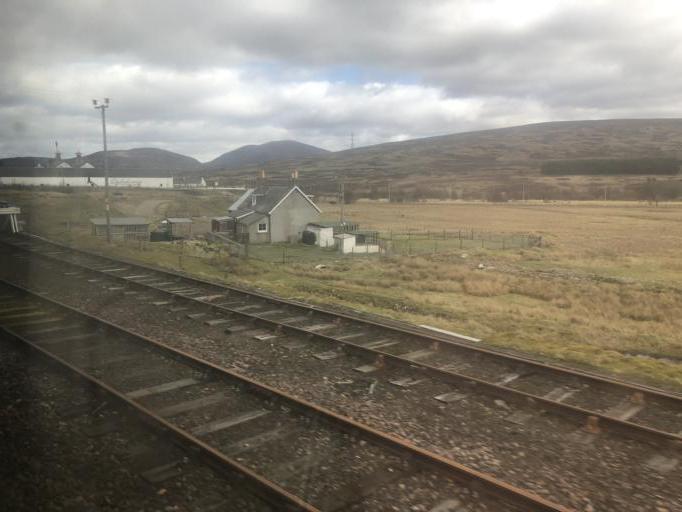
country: GB
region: Scotland
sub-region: Highland
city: Kingussie
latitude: 56.9382
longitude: -4.2437
